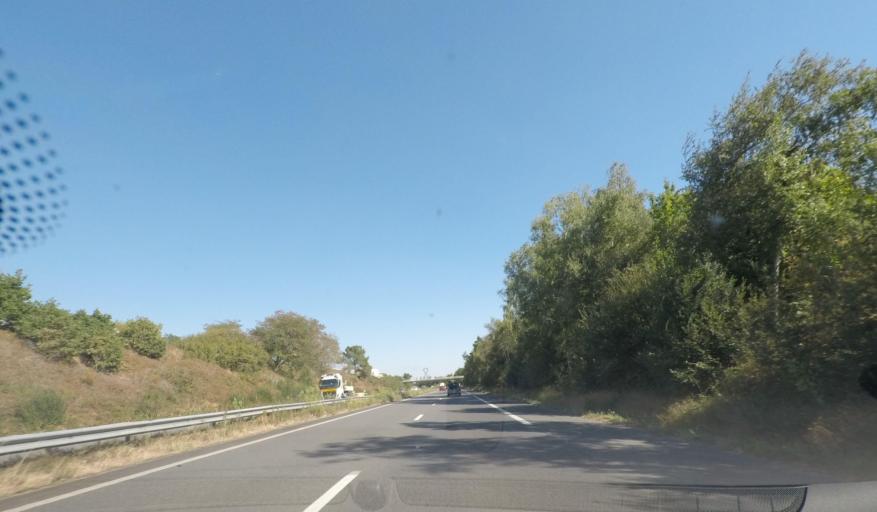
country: FR
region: Pays de la Loire
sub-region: Departement de la Loire-Atlantique
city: Pontchateau
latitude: 47.4506
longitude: -2.1300
